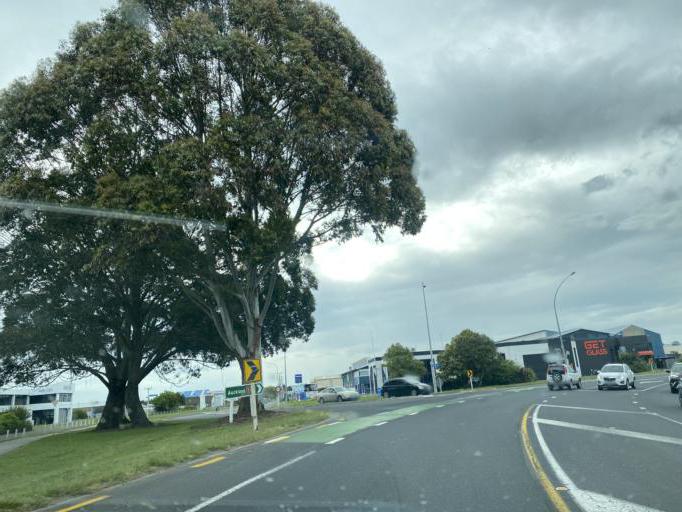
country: NZ
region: Waikato
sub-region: Hamilton City
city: Hamilton
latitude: -37.8054
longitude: 175.2603
